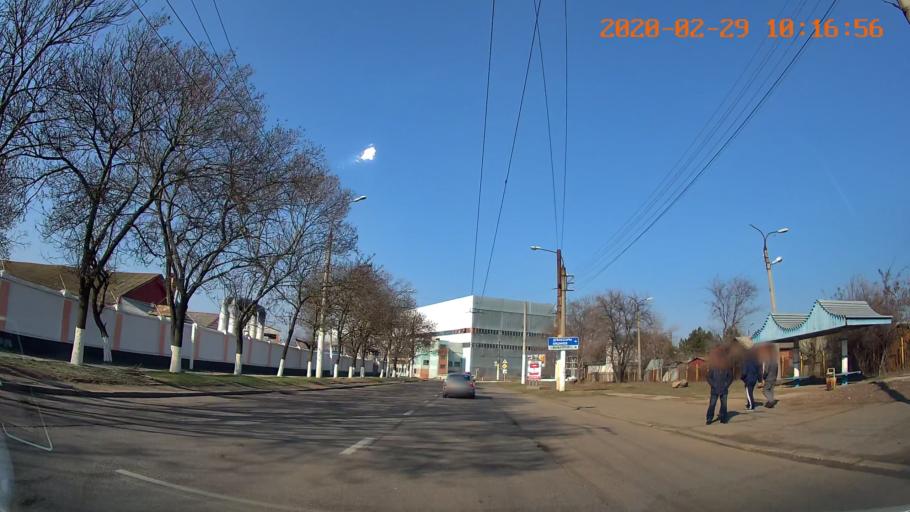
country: MD
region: Telenesti
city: Tiraspolul Nou
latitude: 46.8562
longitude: 29.6241
